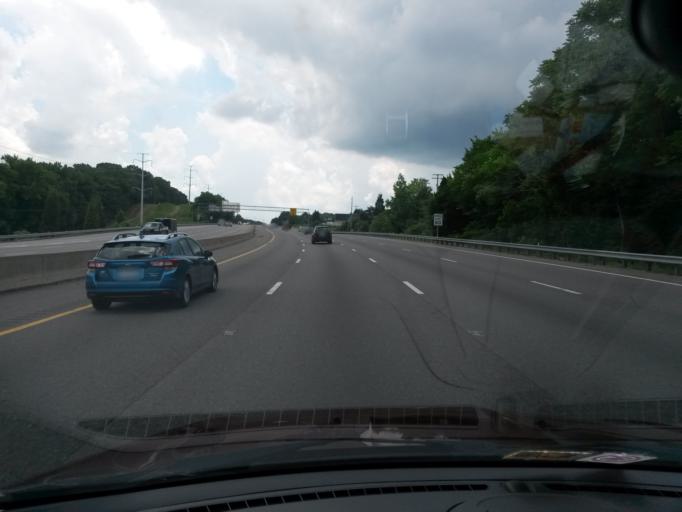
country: US
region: Virginia
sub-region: Chesterfield County
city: Bellwood
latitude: 37.4329
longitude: -77.4318
